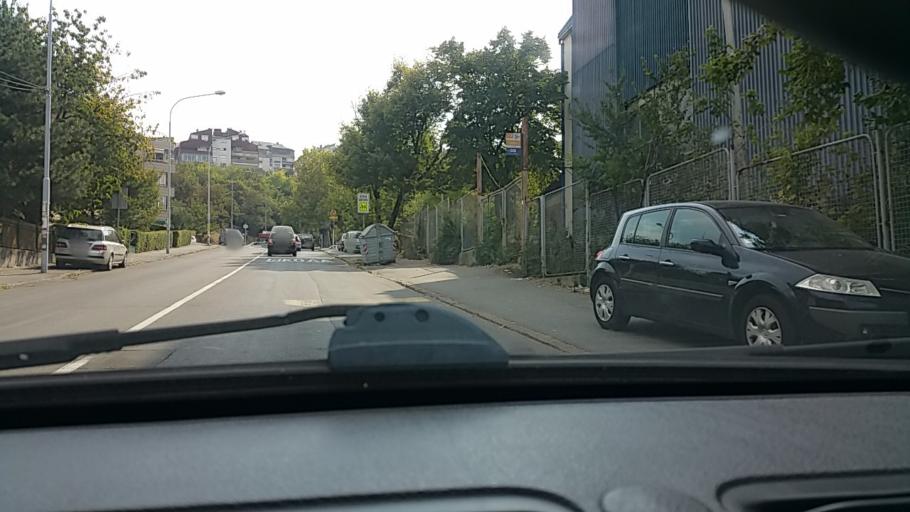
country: RS
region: Central Serbia
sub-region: Belgrade
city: Rakovica
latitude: 44.7497
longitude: 20.4549
